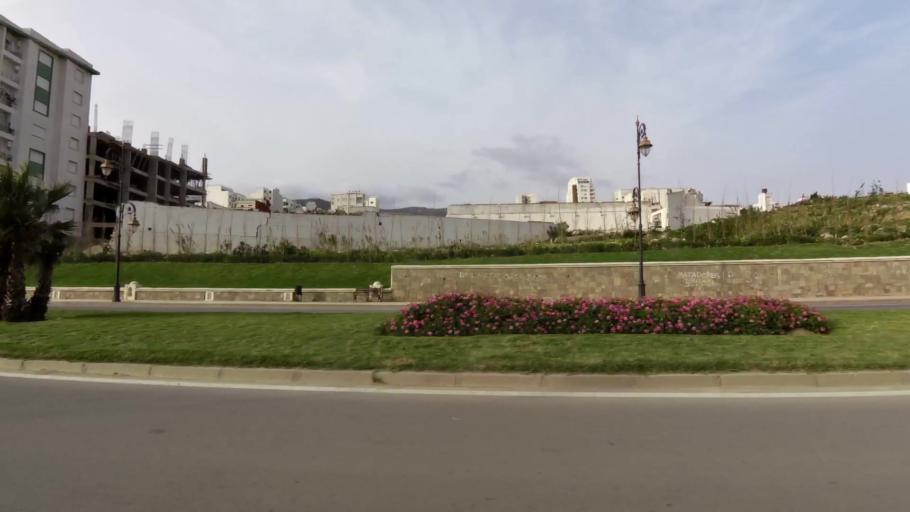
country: MA
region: Tanger-Tetouan
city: Tetouan
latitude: 35.5661
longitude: -5.3841
